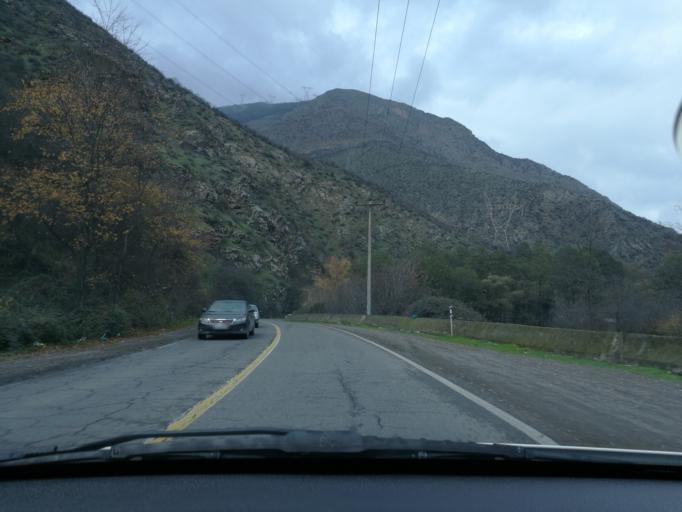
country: IR
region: Mazandaran
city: Chalus
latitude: 36.3451
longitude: 51.2579
